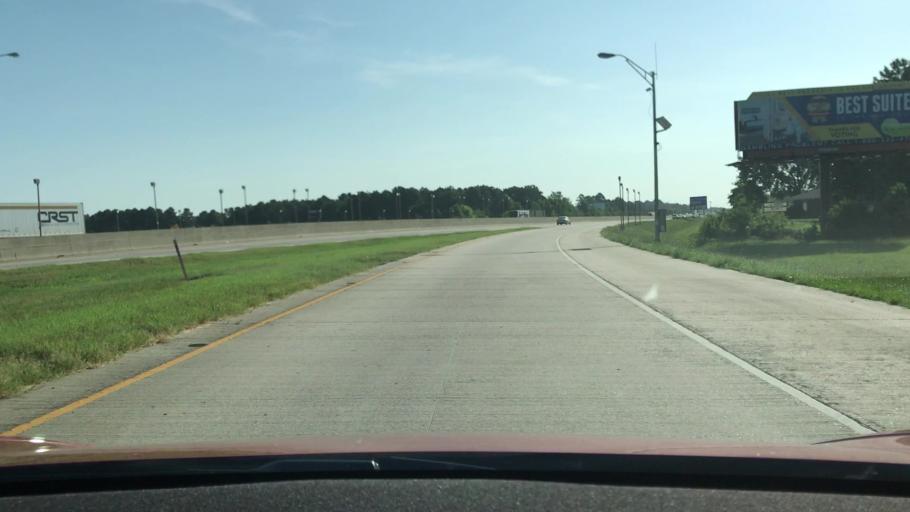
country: US
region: Louisiana
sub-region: Caddo Parish
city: Shreveport
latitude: 32.4567
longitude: -93.8416
